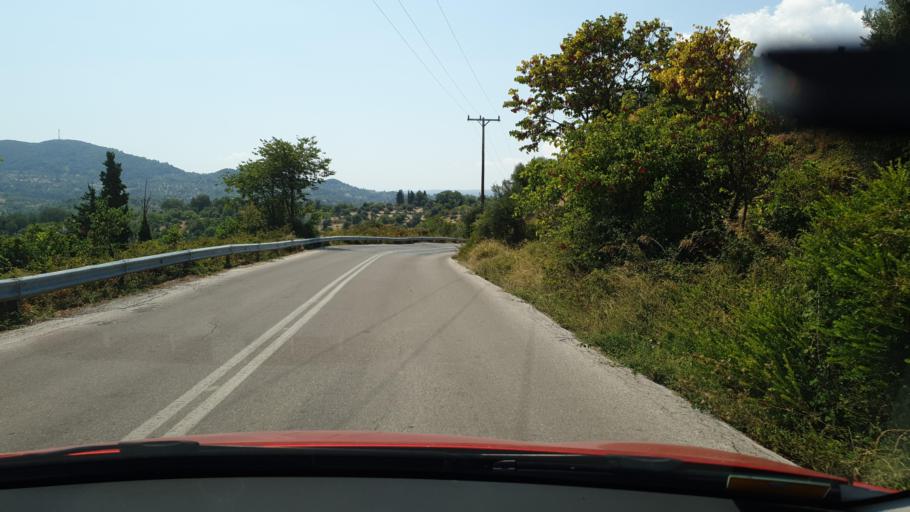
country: GR
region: Central Greece
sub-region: Nomos Evvoias
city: Kymi
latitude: 38.6106
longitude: 24.0793
